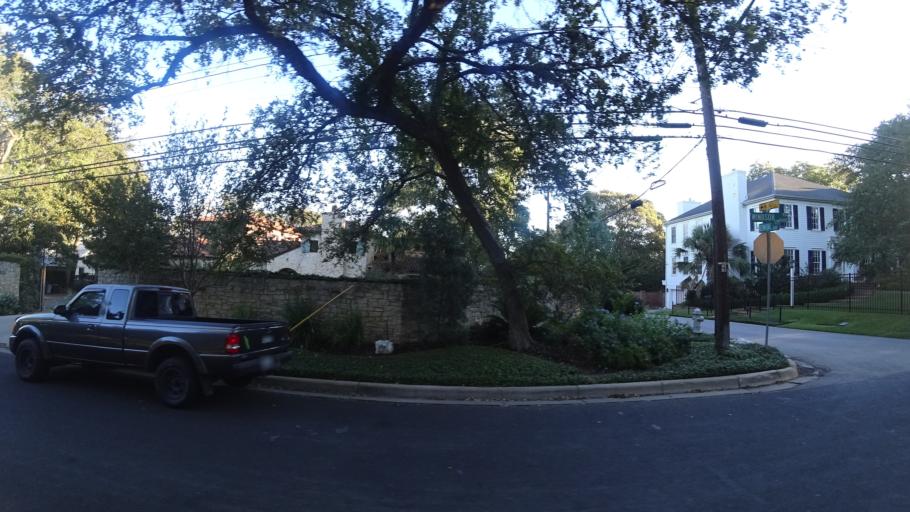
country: US
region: Texas
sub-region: Travis County
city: West Lake Hills
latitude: 30.3011
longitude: -97.7770
